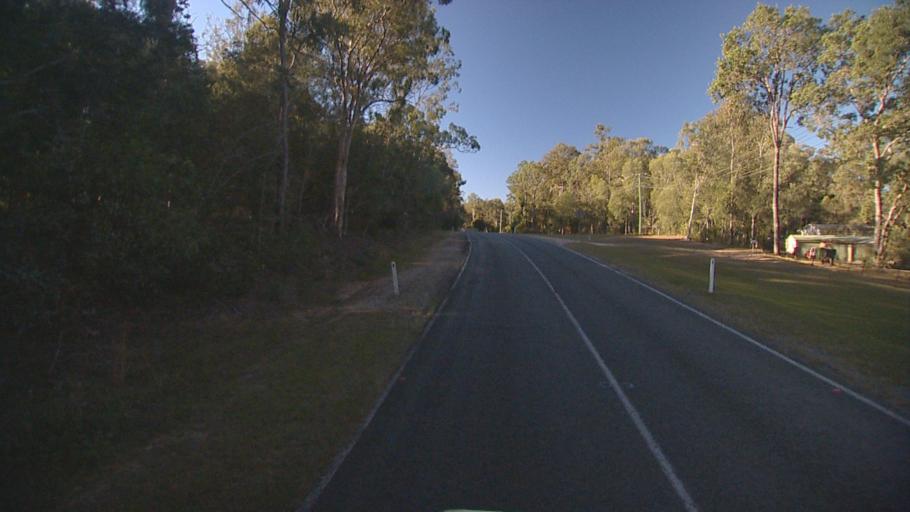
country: AU
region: Queensland
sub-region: Logan
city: Chambers Flat
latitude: -27.7564
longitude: 153.0491
